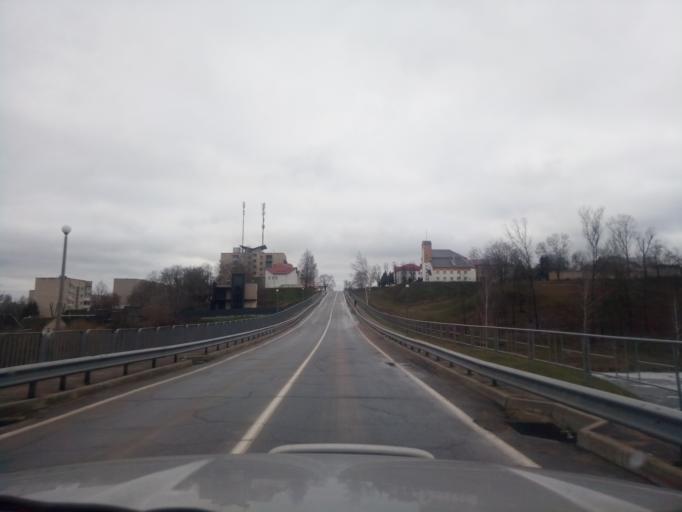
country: BY
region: Minsk
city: Kapyl'
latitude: 53.1532
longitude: 27.0954
